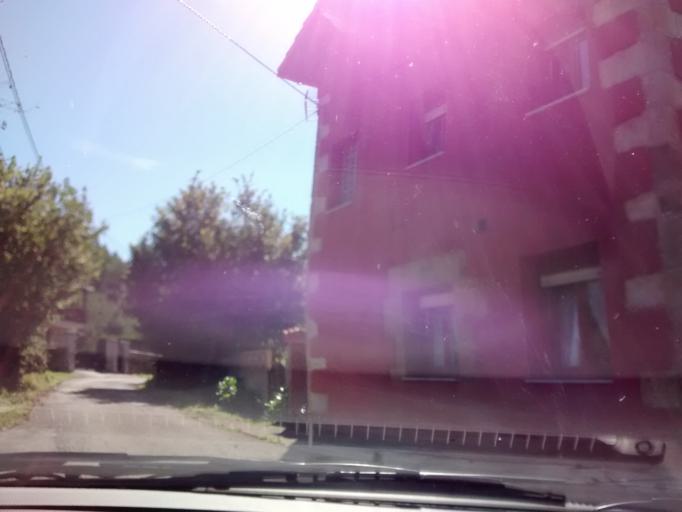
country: ES
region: Cantabria
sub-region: Provincia de Cantabria
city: Entrambasaguas
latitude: 43.3643
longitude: -3.7146
